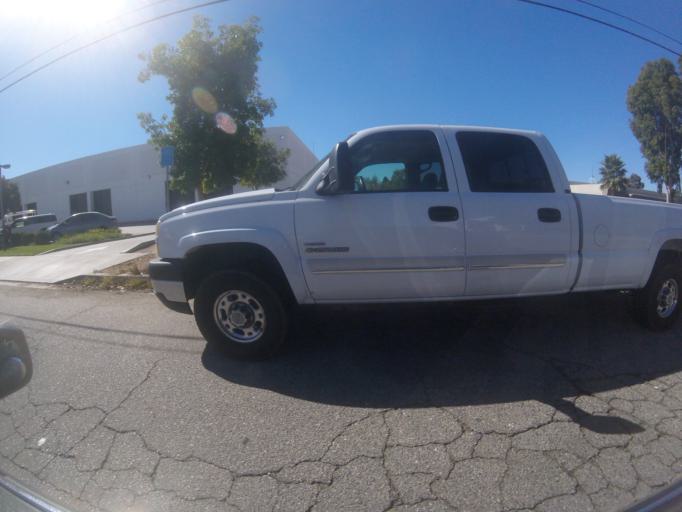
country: US
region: California
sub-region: San Bernardino County
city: Redlands
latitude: 34.0615
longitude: -117.2218
